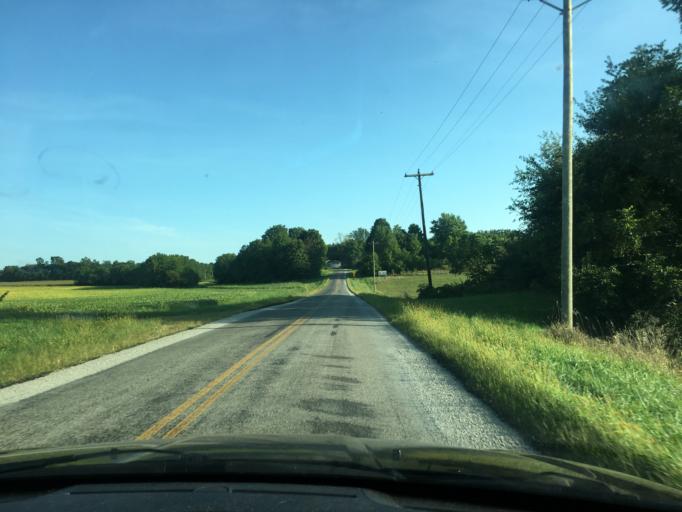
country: US
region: Ohio
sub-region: Logan County
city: West Liberty
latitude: 40.2061
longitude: -83.6677
